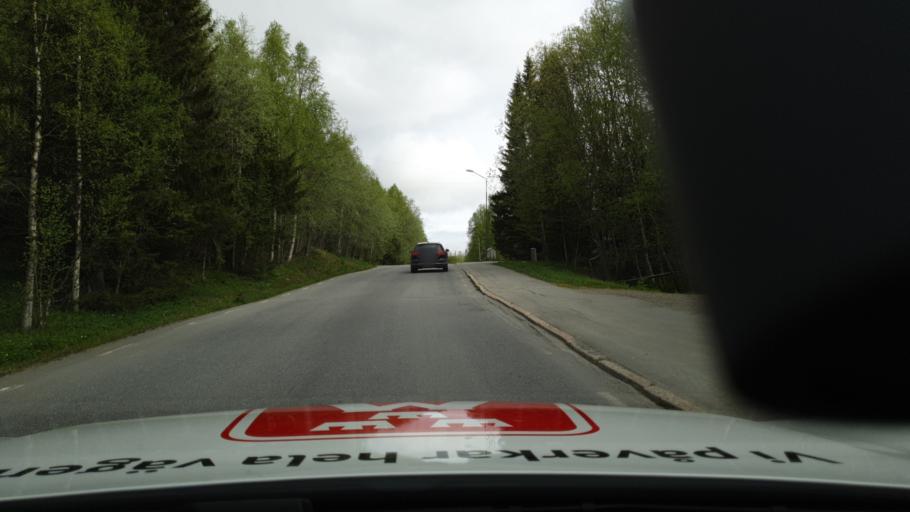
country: NO
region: Nord-Trondelag
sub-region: Lierne
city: Sandvika
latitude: 64.4965
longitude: 14.1405
